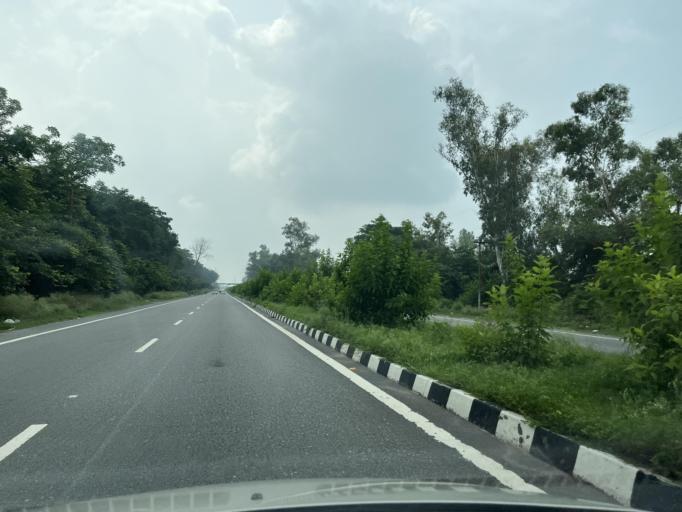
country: IN
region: Uttarakhand
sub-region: Dehradun
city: Doiwala
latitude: 30.1103
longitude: 78.1708
